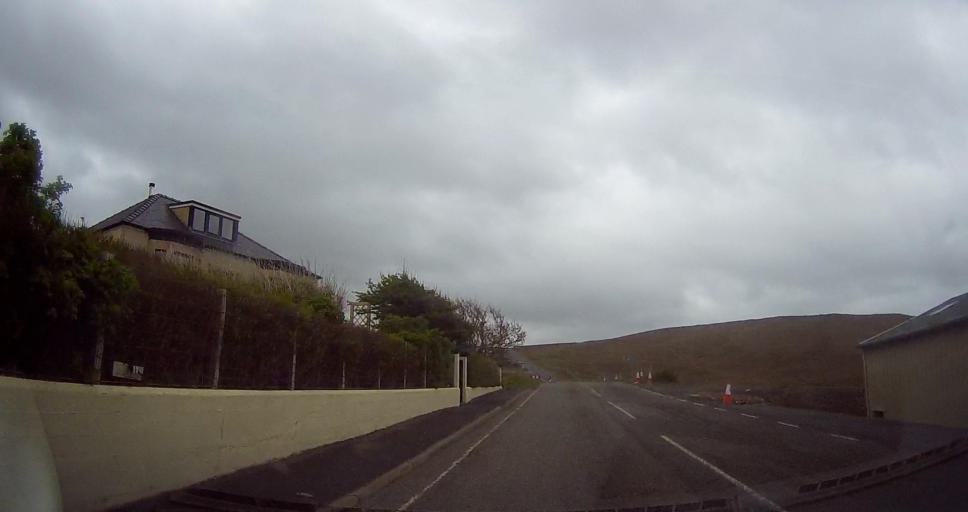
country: GB
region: Scotland
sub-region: Shetland Islands
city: Lerwick
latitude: 60.4894
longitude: -1.4515
